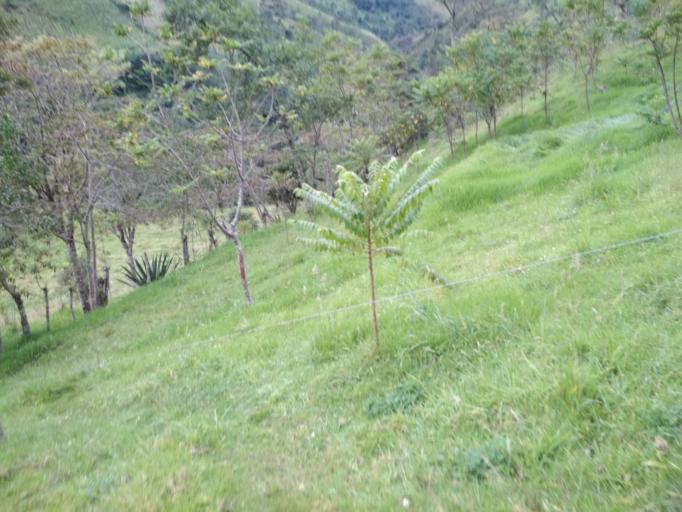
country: CO
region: Cauca
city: Jambalo
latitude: 2.7391
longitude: -76.3467
